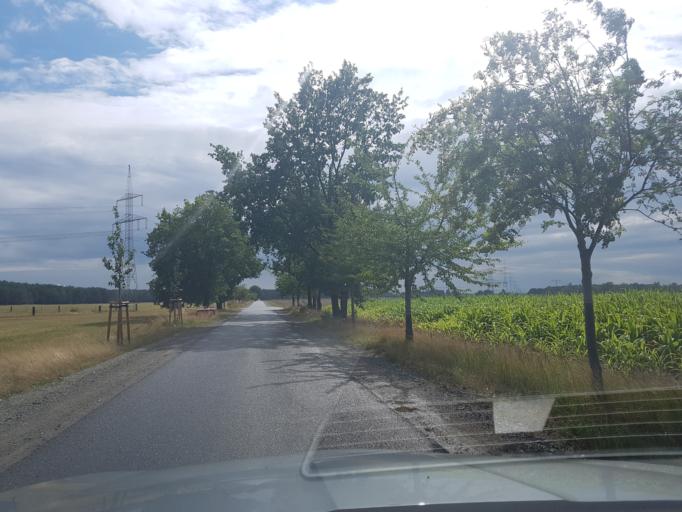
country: DE
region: Brandenburg
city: Sonnewalde
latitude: 51.6619
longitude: 13.6384
